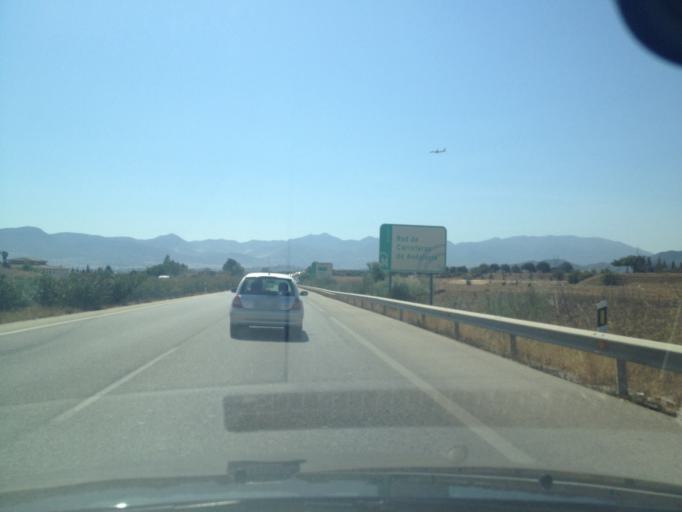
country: ES
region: Andalusia
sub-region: Provincia de Malaga
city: Estacion de Cartama
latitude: 36.7297
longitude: -4.5512
